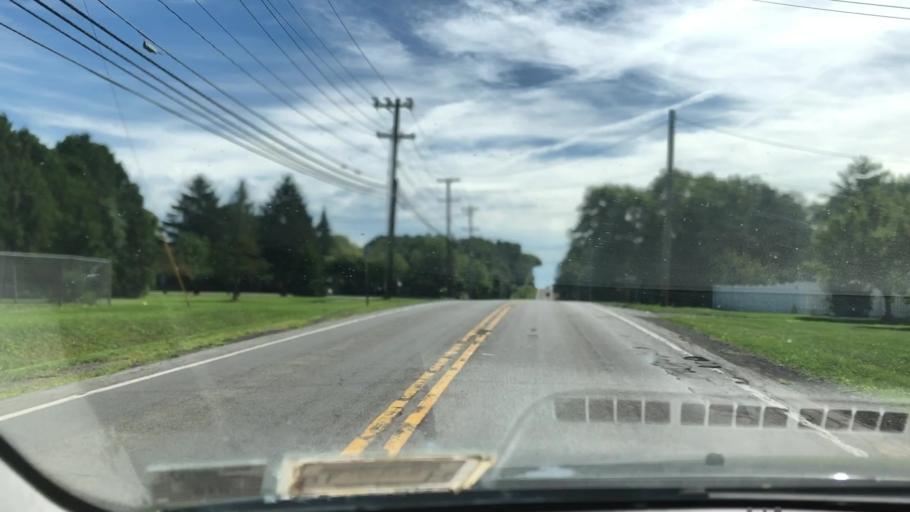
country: US
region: New York
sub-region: Monroe County
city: Fairport
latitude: 43.1084
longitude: -77.4239
